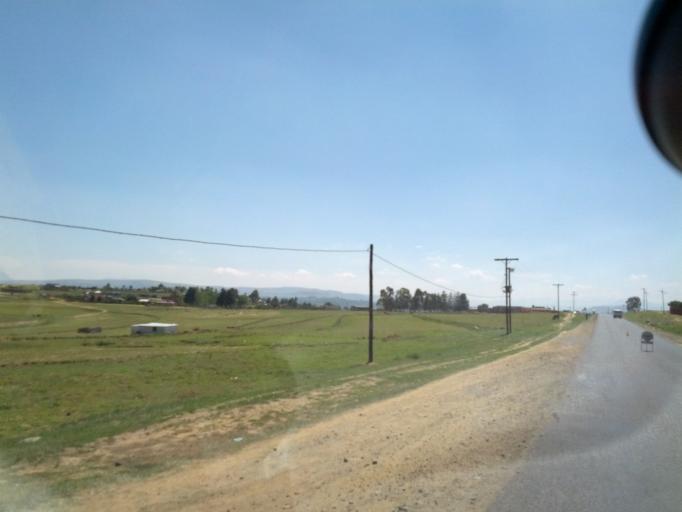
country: LS
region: Butha-Buthe
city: Butha-Buthe
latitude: -28.7802
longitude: 28.2277
